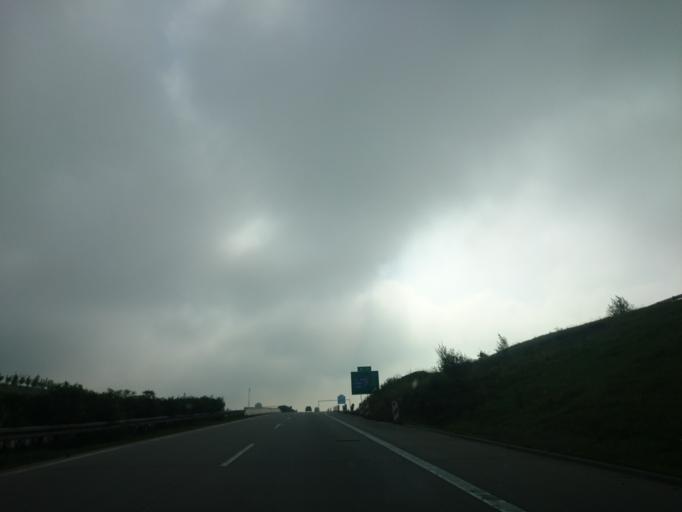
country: CZ
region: Olomoucky
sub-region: Okres Prerov
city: Lipnik nad Becvou
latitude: 49.5475
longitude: 17.5757
